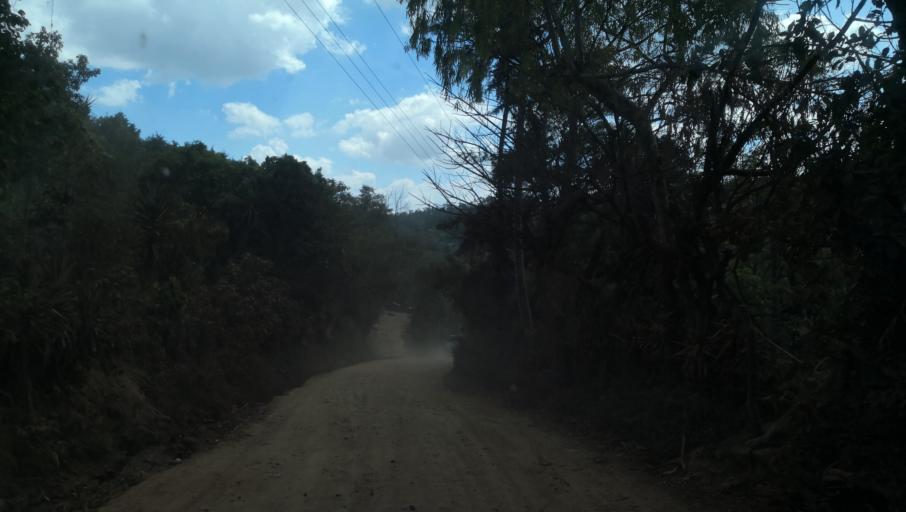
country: GT
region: Jalapa
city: San Carlos Alzatate
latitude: 14.3976
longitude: -89.9920
